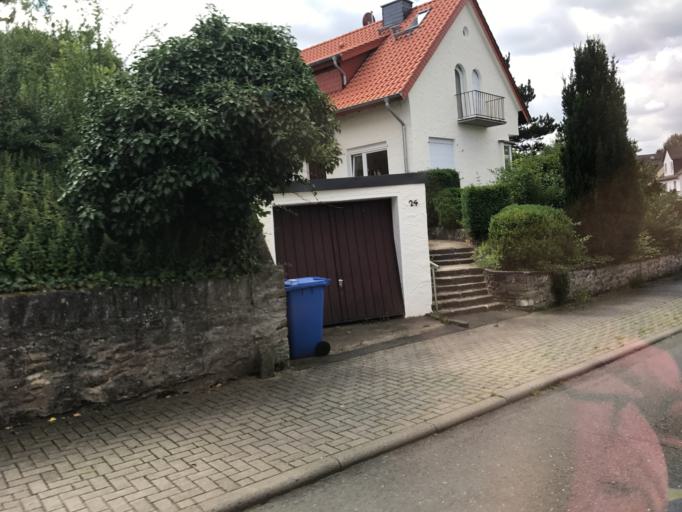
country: DE
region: Hesse
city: Weilburg
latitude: 50.4844
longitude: 8.2721
